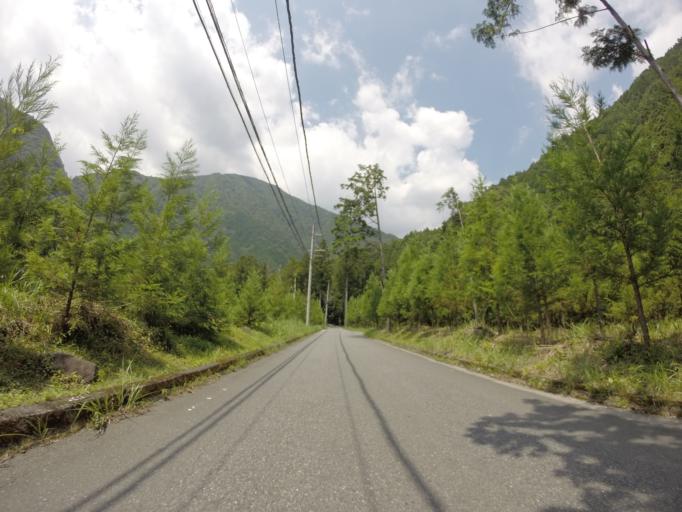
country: JP
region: Shizuoka
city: Shizuoka-shi
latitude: 35.2580
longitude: 138.3305
